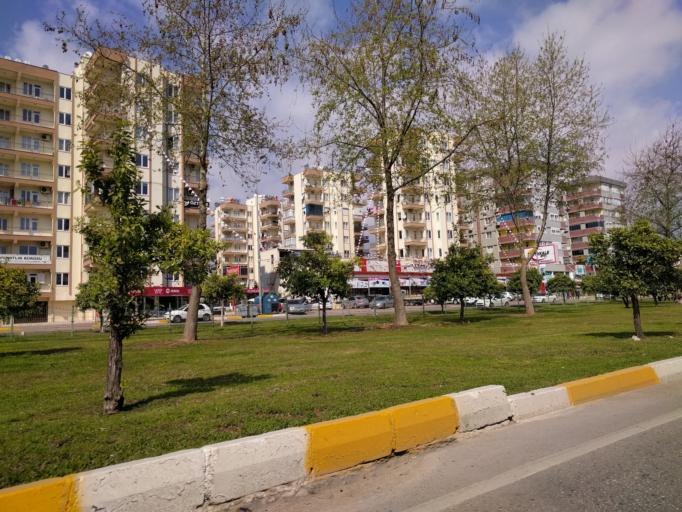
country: TR
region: Antalya
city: Antalya
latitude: 36.9003
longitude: 30.6571
